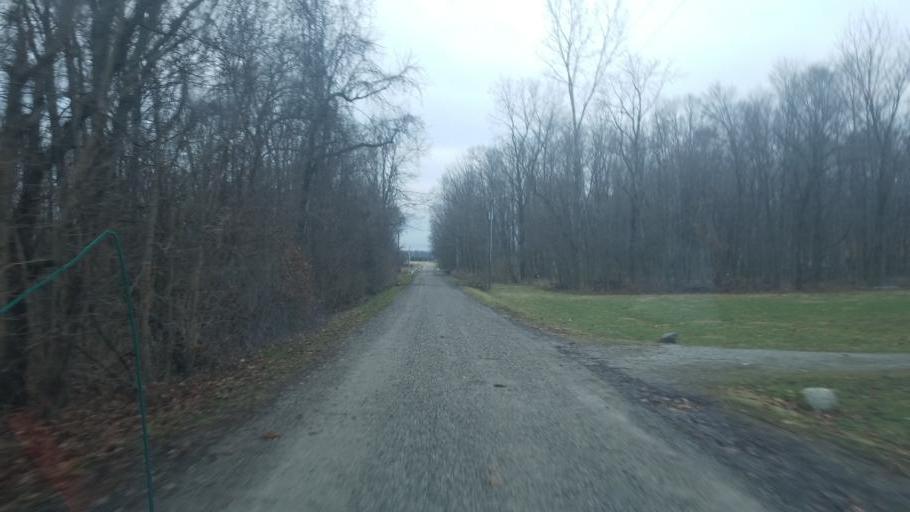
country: US
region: Ohio
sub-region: Morrow County
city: Mount Gilead
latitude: 40.6197
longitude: -82.8997
